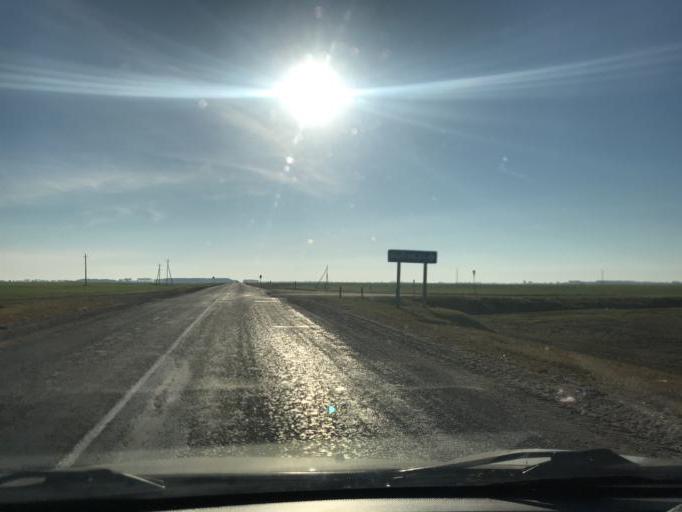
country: BY
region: Gomel
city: Khoyniki
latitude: 51.8354
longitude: 30.0469
